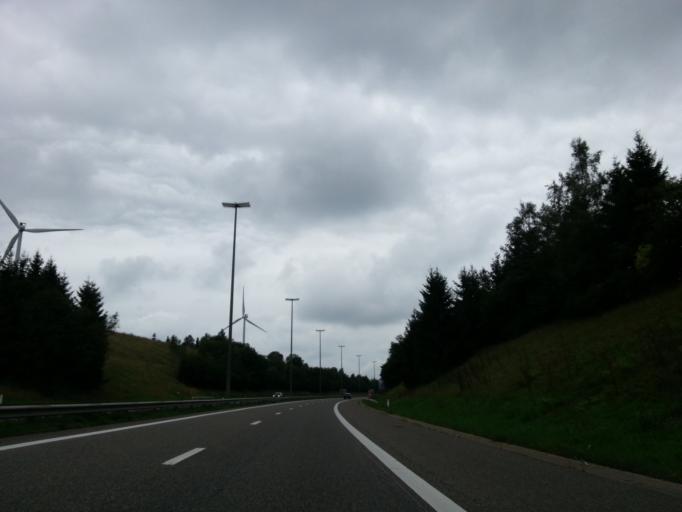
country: BE
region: Wallonia
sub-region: Province de Liege
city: Saint-Vith
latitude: 50.3040
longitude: 6.0790
